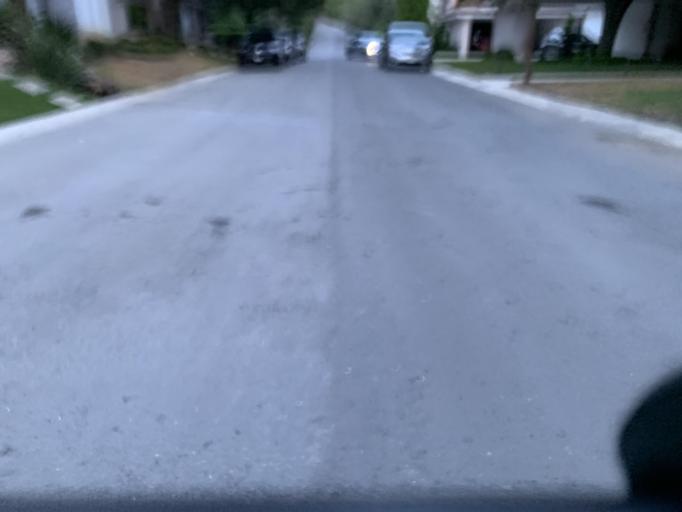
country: MX
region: Nuevo Leon
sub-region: Juarez
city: Bosques de San Pedro
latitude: 25.5158
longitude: -100.1905
